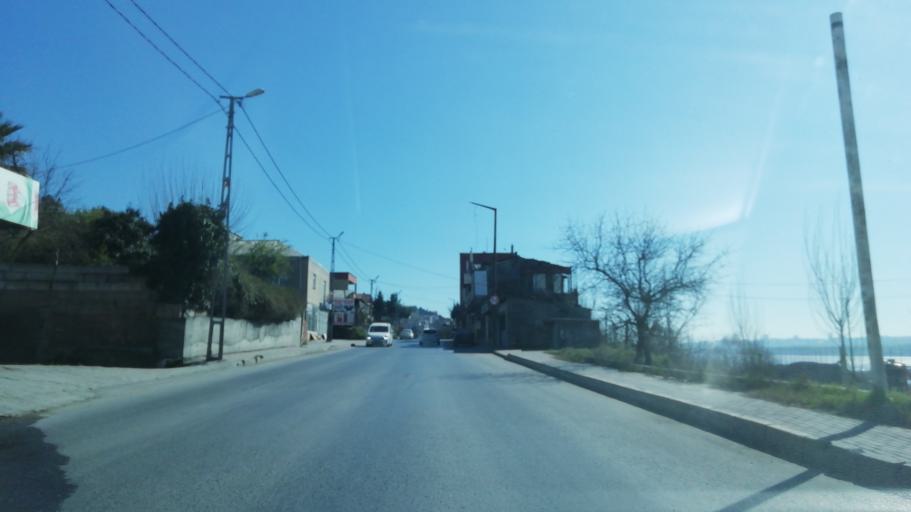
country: TR
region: Istanbul
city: Basaksehir
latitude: 41.0586
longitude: 28.7491
